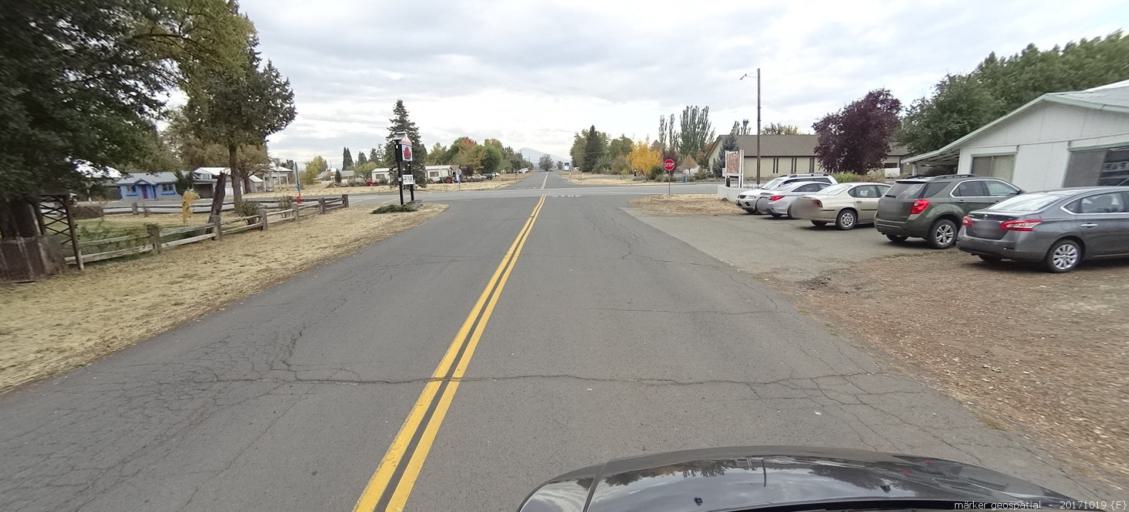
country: US
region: California
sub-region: Shasta County
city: Burney
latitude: 41.0506
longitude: -121.4008
